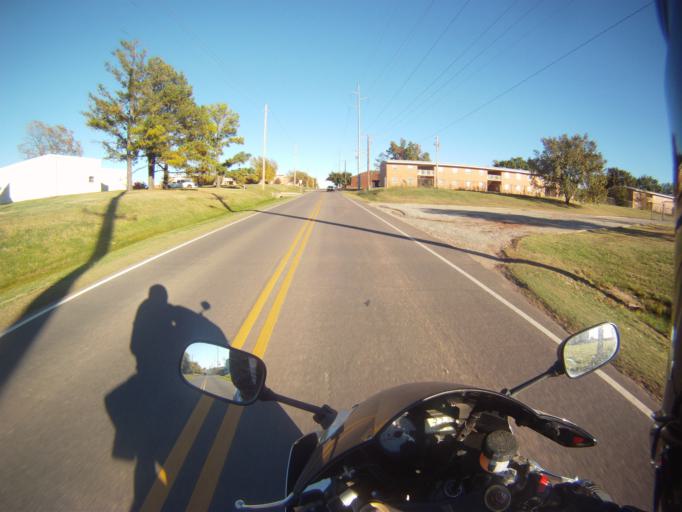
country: US
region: Oklahoma
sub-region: Payne County
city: Stillwater
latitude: 36.1304
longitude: -97.0812
